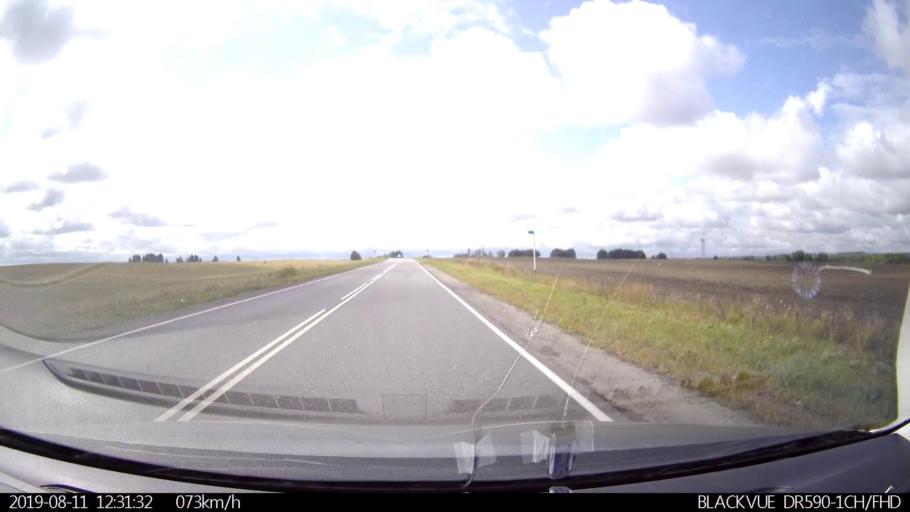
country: RU
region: Ulyanovsk
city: Ignatovka
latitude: 53.8189
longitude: 47.8828
